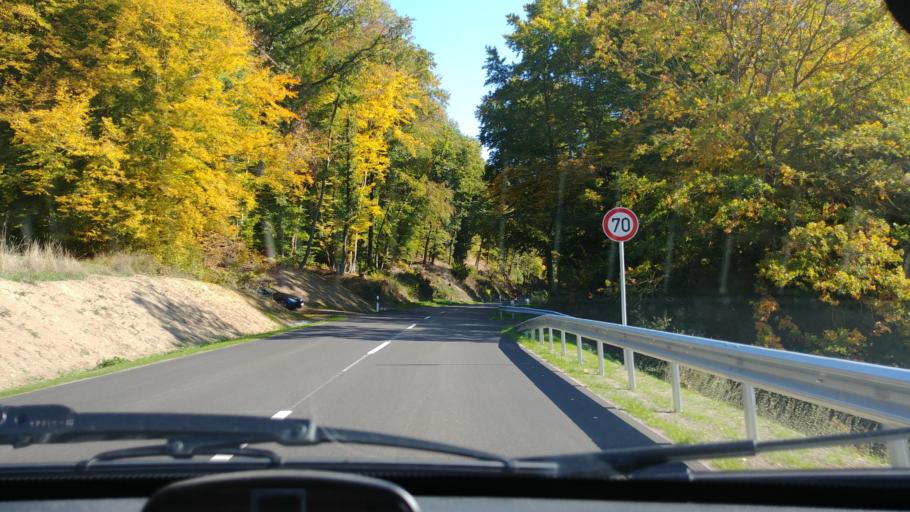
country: DE
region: Rheinland-Pfalz
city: Mudershausen
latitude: 50.2869
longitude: 8.0435
